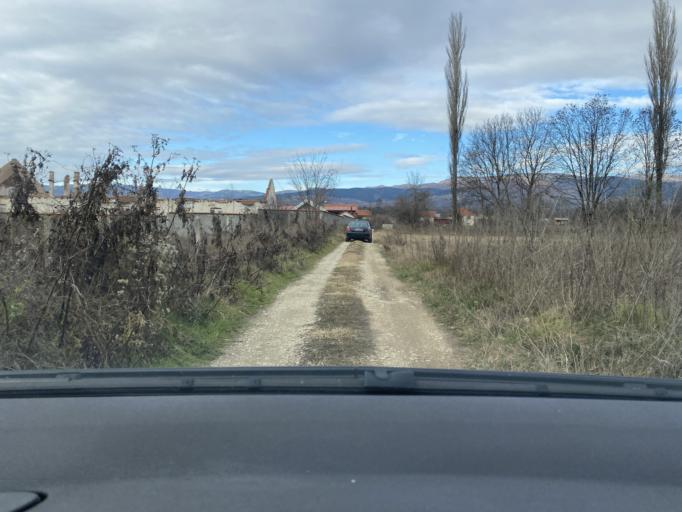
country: MK
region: Opstina Rankovce
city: Rankovce
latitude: 42.1669
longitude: 22.1577
